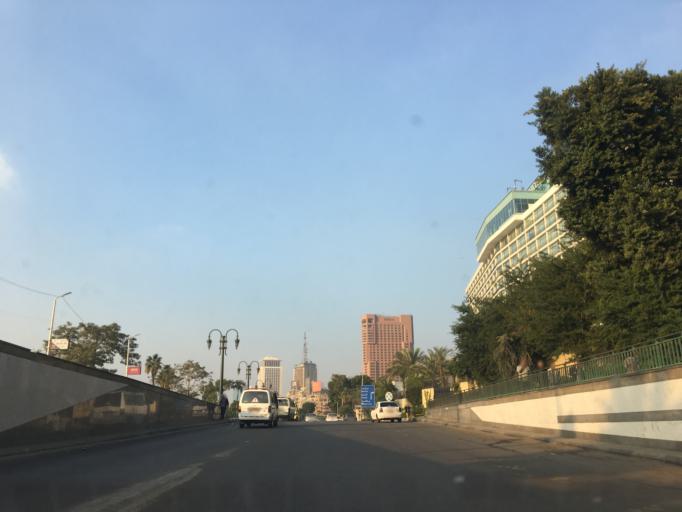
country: EG
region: Muhafazat al Qahirah
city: Cairo
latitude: 30.0446
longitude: 31.2318
